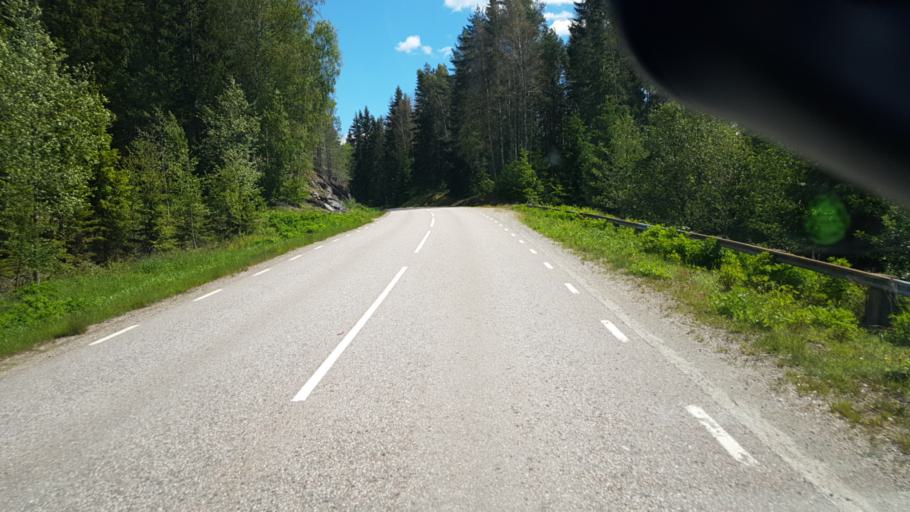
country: SE
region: Vaermland
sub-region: Arvika Kommun
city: Arvika
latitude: 59.6263
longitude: 12.8606
